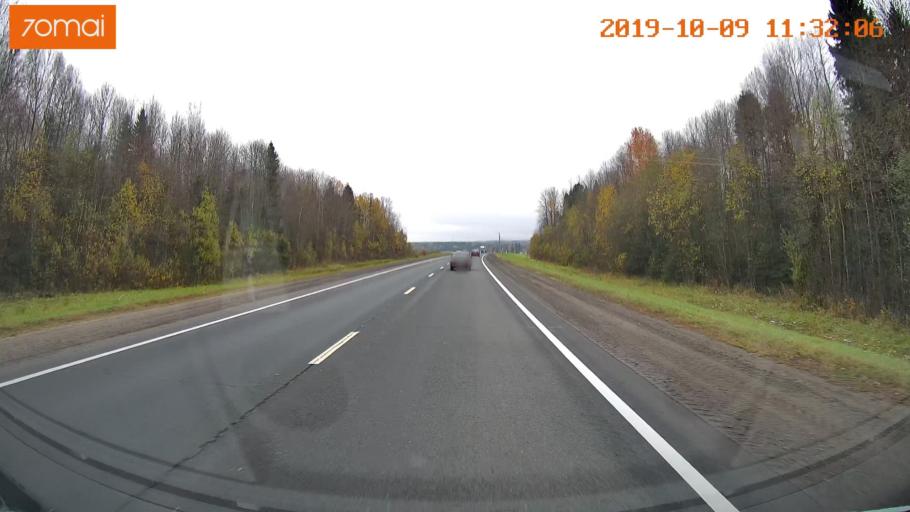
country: RU
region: Vologda
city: Gryazovets
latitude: 59.0393
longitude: 40.1055
